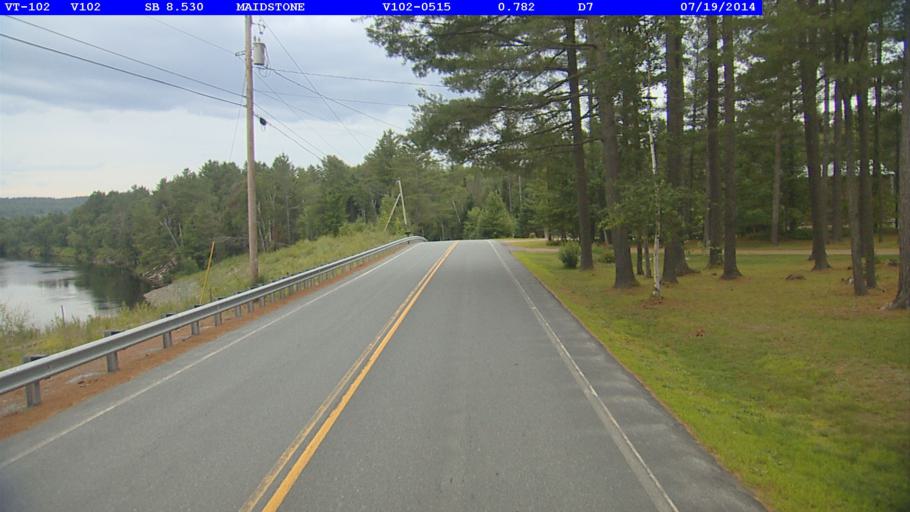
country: US
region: Vermont
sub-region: Essex County
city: Guildhall
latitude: 44.5818
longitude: -71.5550
